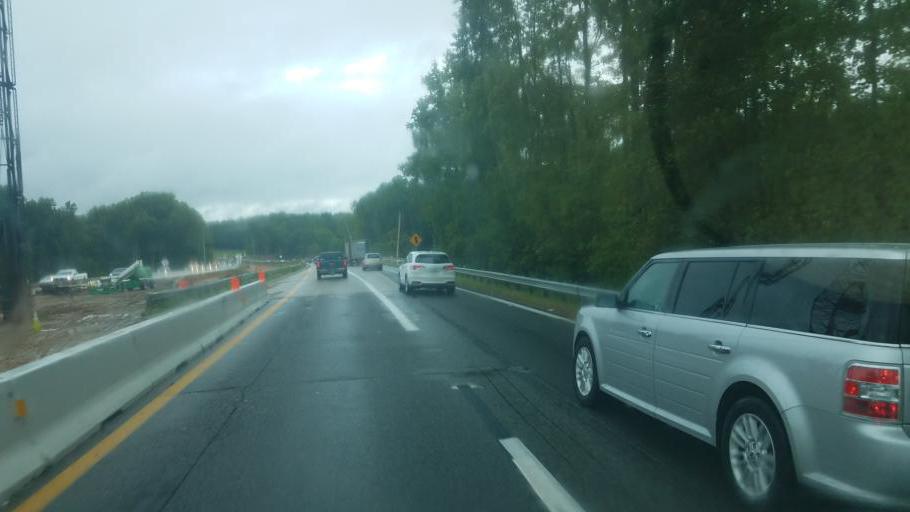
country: US
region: Virginia
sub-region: York County
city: Yorktown
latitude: 37.2132
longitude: -76.5878
